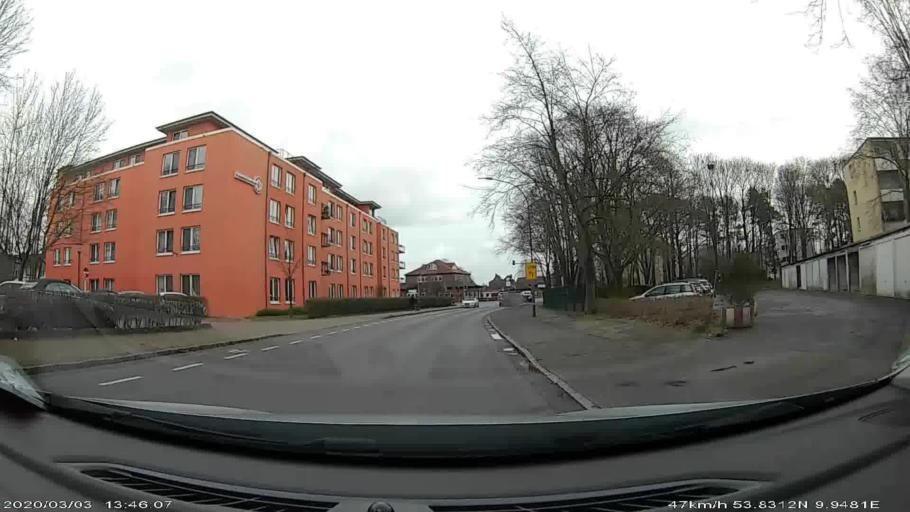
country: DE
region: Schleswig-Holstein
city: Kaltenkirchen
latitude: 53.8317
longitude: 9.9490
